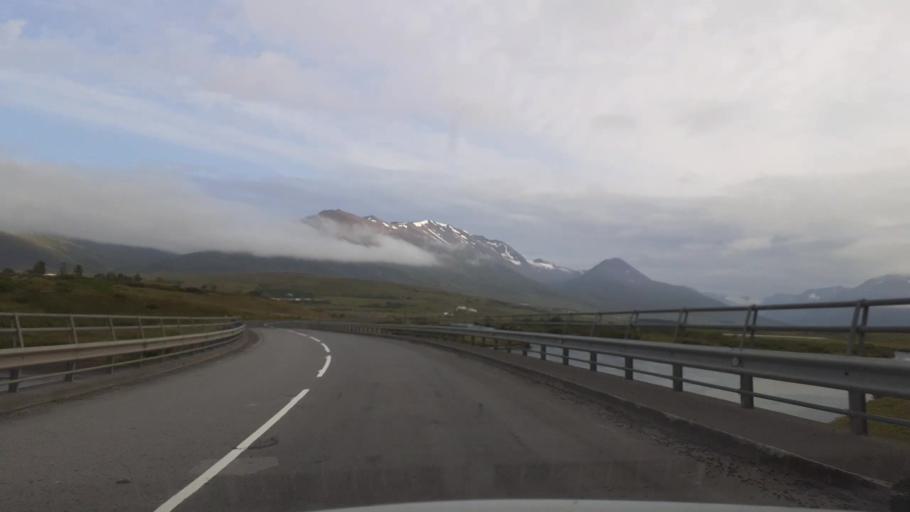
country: IS
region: Northeast
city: Dalvik
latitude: 65.9605
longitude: -18.5389
